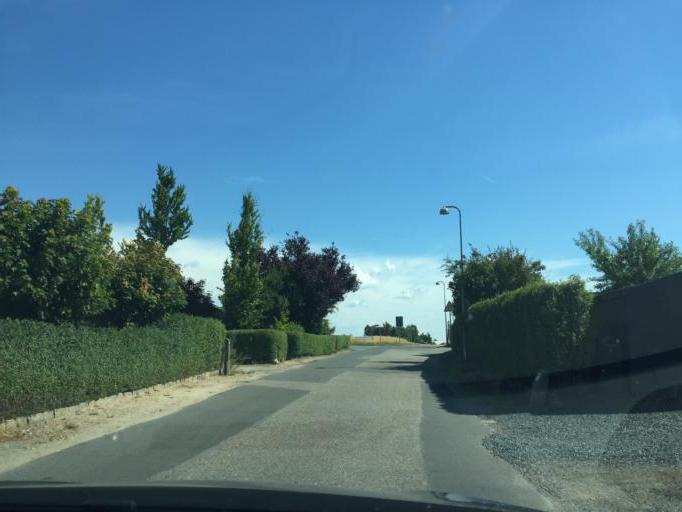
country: DK
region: South Denmark
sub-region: Odense Kommune
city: Bellinge
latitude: 55.3384
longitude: 10.3605
